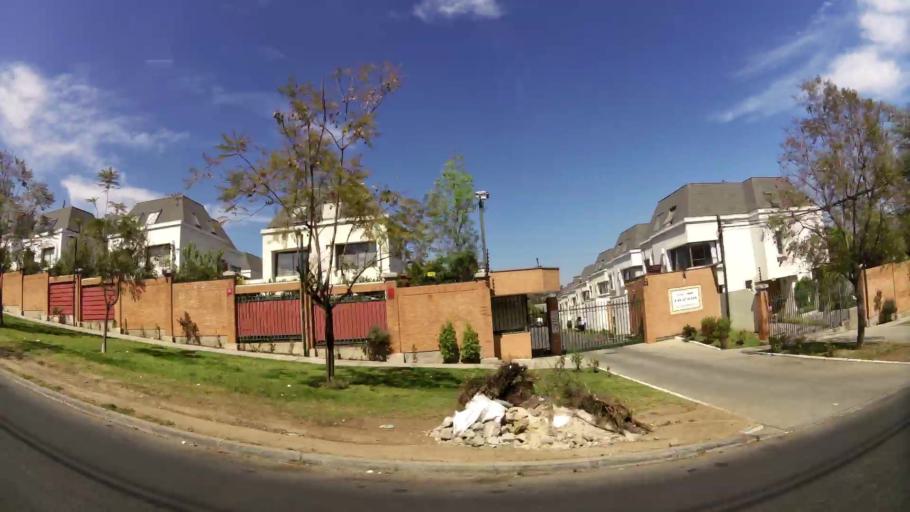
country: CL
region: Santiago Metropolitan
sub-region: Provincia de Santiago
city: Villa Presidente Frei, Nunoa, Santiago, Chile
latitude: -33.4528
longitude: -70.5270
